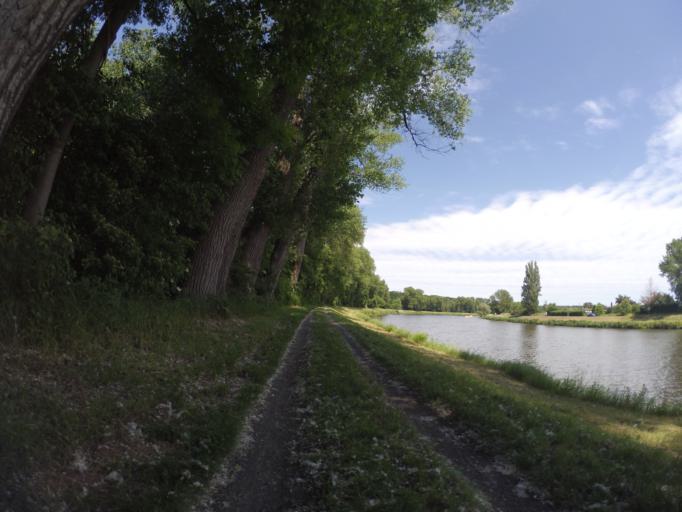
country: CZ
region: Central Bohemia
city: Poricany
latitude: 50.1712
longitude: 14.9278
